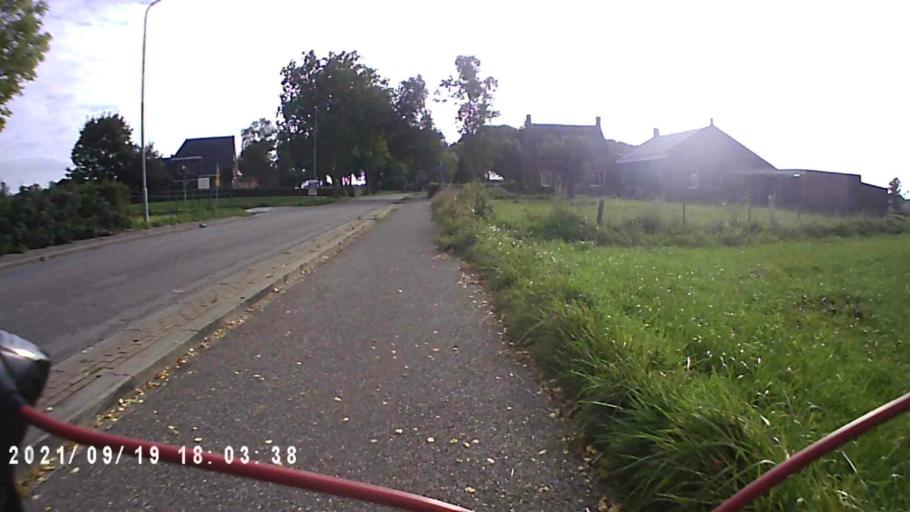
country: NL
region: Groningen
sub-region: Gemeente Delfzijl
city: Delfzijl
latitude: 53.2468
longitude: 6.9271
